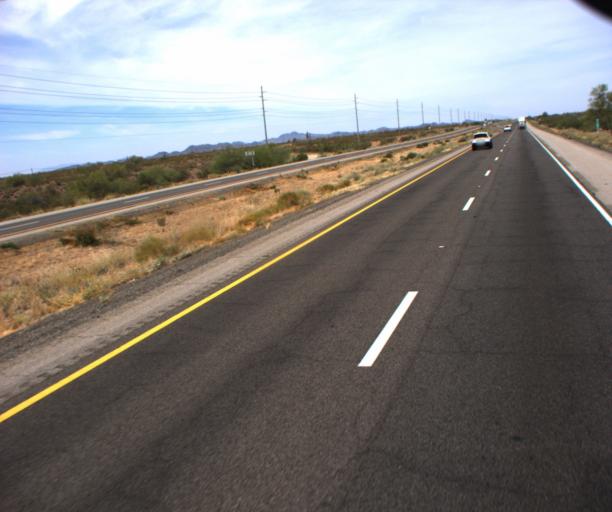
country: US
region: Arizona
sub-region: Maricopa County
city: Sun City West
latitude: 33.7943
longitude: -112.5495
